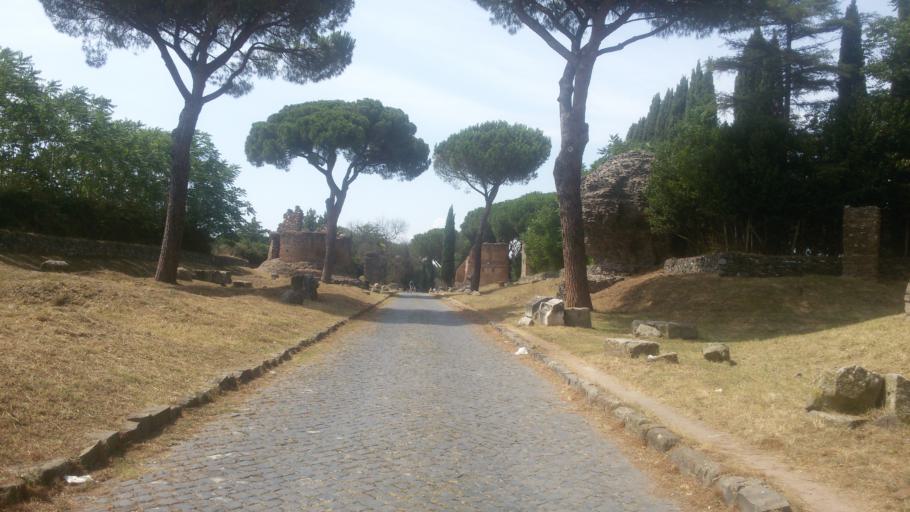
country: IT
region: Latium
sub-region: Citta metropolitana di Roma Capitale
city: Borgo Lotti
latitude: 41.8311
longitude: 12.5442
